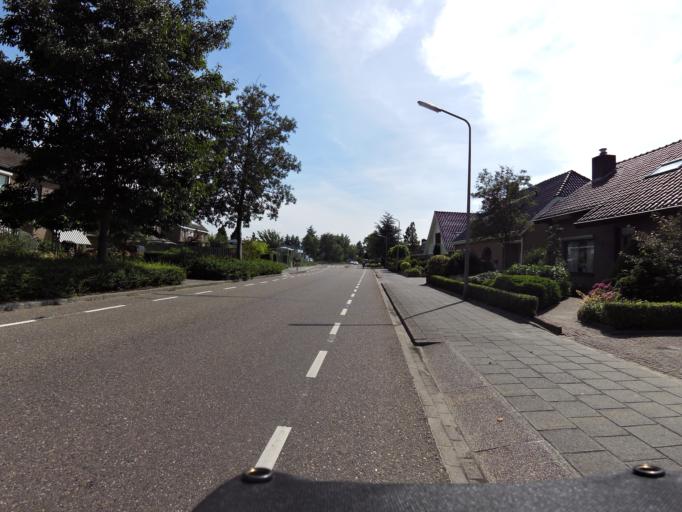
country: NL
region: South Holland
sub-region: Gemeente Goeree-Overflakkee
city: Middelharnis
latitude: 51.7527
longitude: 4.1506
